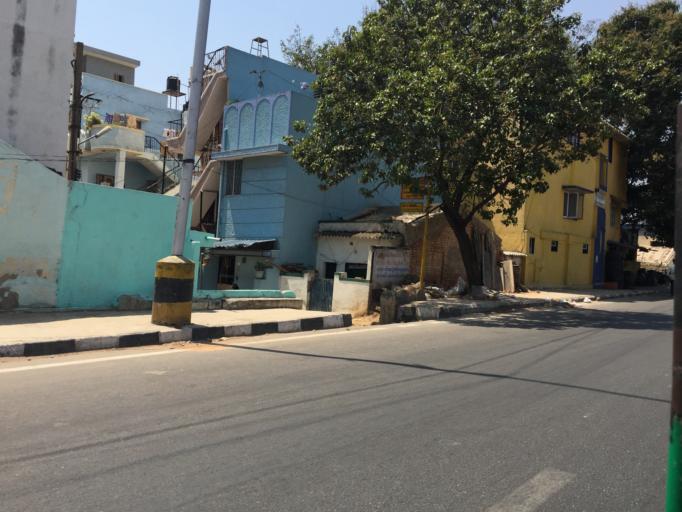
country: IN
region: Karnataka
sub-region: Bangalore Urban
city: Bangalore
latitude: 12.9819
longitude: 77.6275
